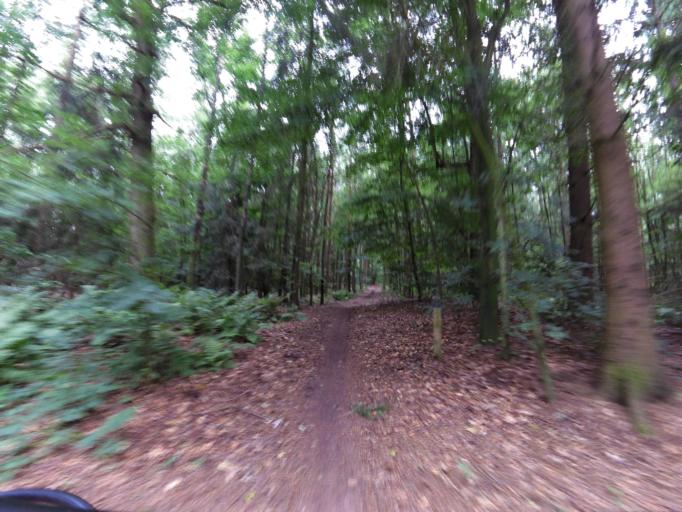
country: NL
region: North Brabant
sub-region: Gemeente Son en Breugel
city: Breugel
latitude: 51.5512
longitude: 5.5211
